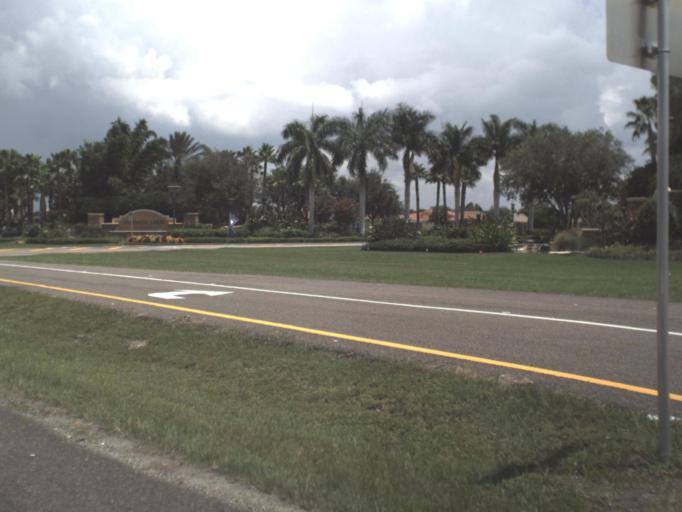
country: US
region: Florida
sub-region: Hillsborough County
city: Sun City Center
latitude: 27.7338
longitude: -82.3352
